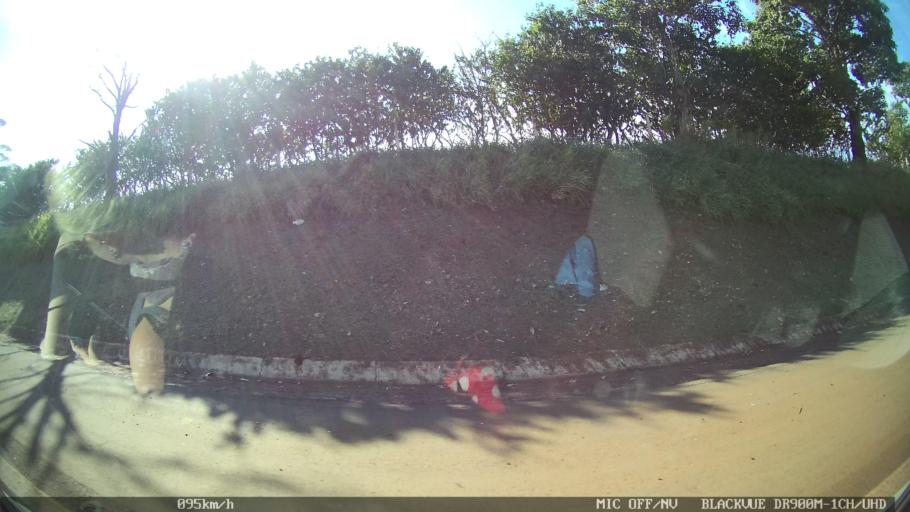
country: BR
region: Sao Paulo
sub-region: Iracemapolis
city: Iracemapolis
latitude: -22.6693
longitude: -47.5476
